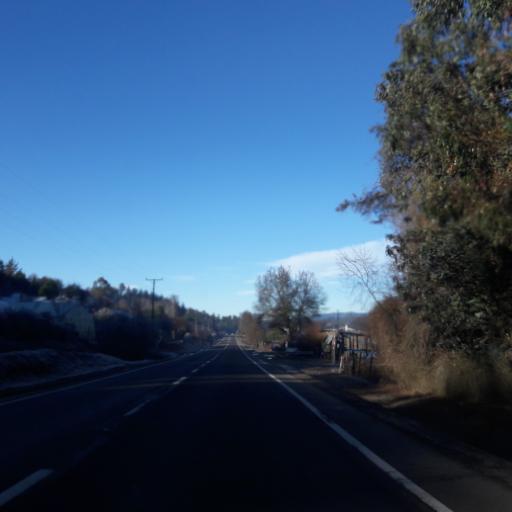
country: CL
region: Biobio
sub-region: Provincia de Biobio
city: La Laja
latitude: -37.3054
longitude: -72.9263
